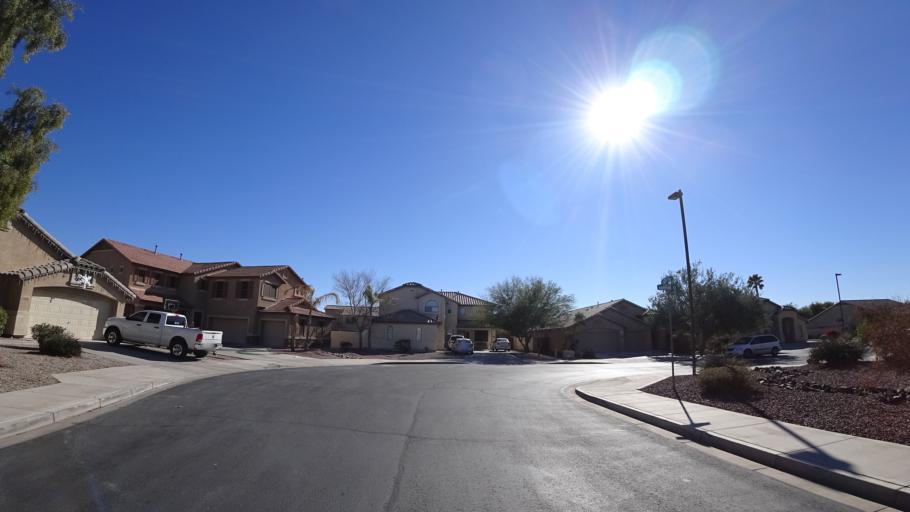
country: US
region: Arizona
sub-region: Maricopa County
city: Goodyear
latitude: 33.4235
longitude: -112.4069
